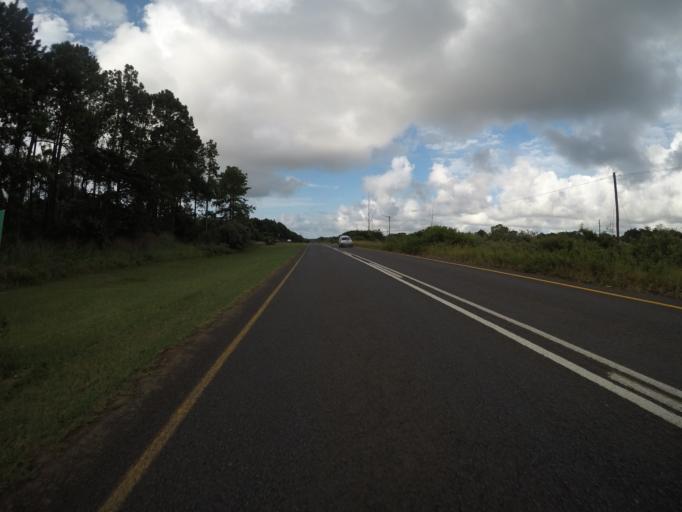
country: ZA
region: KwaZulu-Natal
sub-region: uMkhanyakude District Municipality
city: Mtubatuba
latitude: -28.3783
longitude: 32.2495
